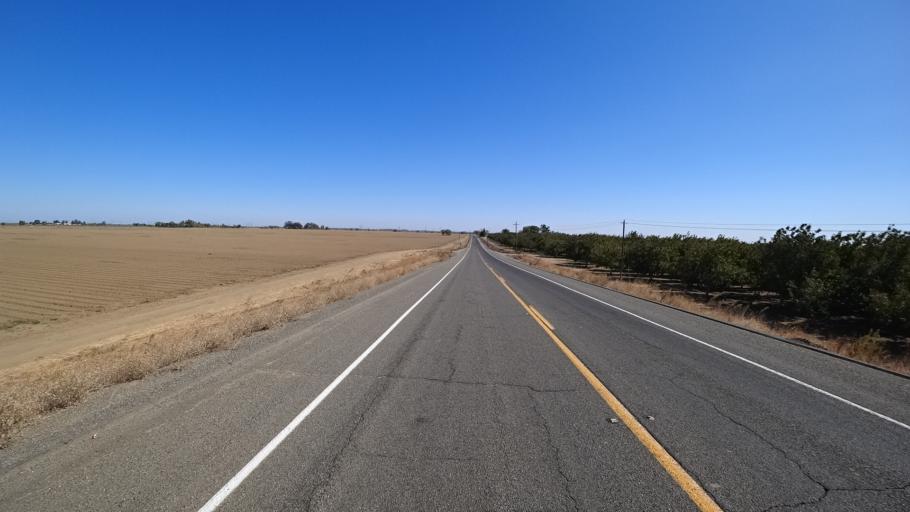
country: US
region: California
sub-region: Yolo County
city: Winters
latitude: 38.5618
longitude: -121.9516
